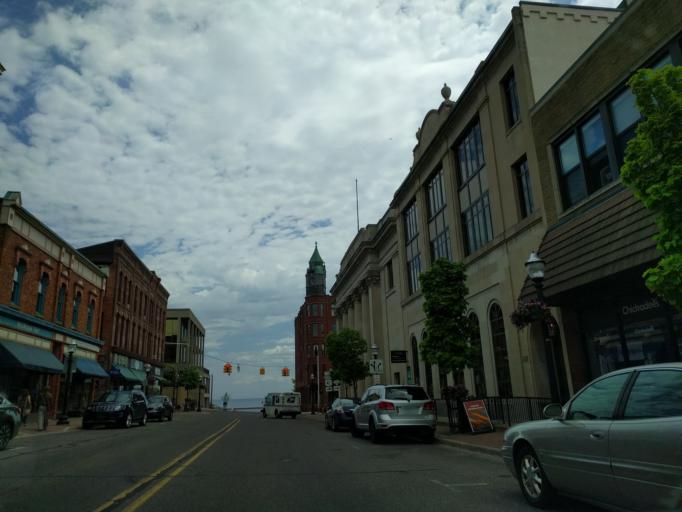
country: US
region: Michigan
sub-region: Marquette County
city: Marquette
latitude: 46.5433
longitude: -87.3939
